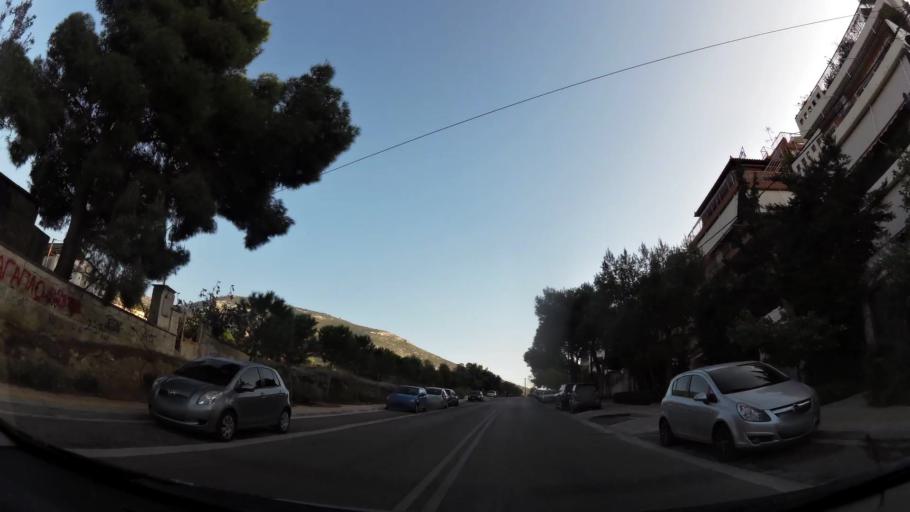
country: GR
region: Attica
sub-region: Nomarchia Athinas
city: Argyroupoli
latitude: 37.8927
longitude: 23.7766
